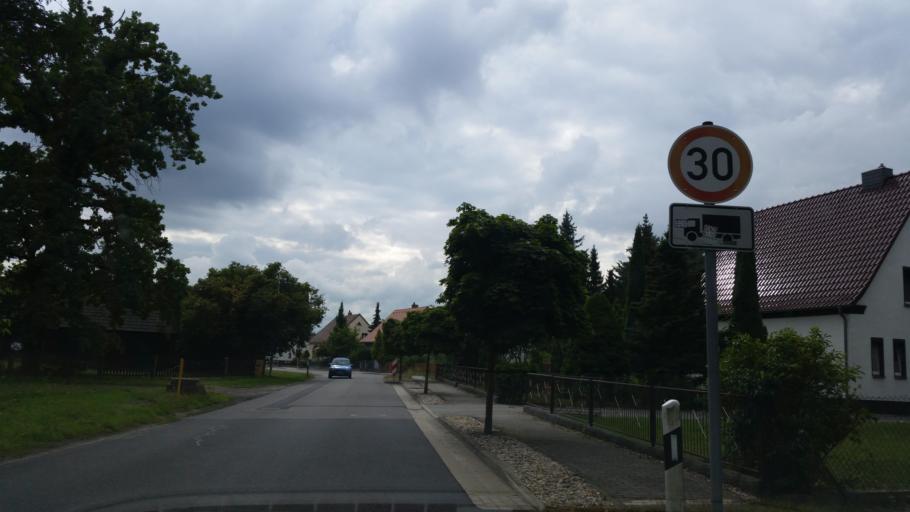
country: DE
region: Saxony
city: Klitten
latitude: 51.3883
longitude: 14.6219
